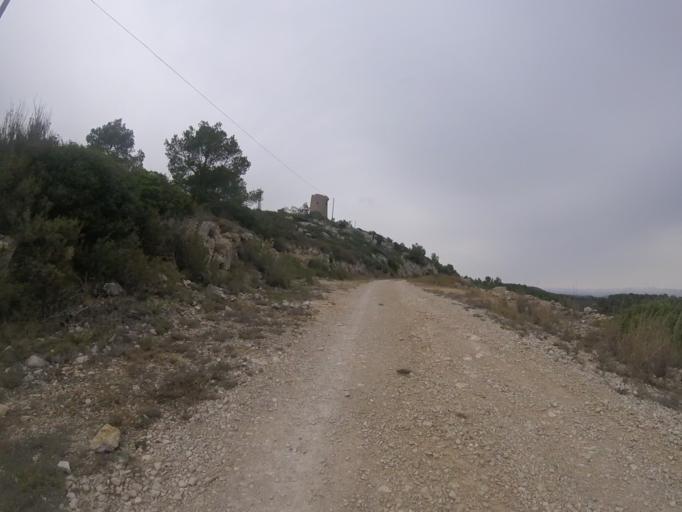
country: ES
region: Valencia
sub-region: Provincia de Castello
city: Alcoceber
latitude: 40.2796
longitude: 0.2831
